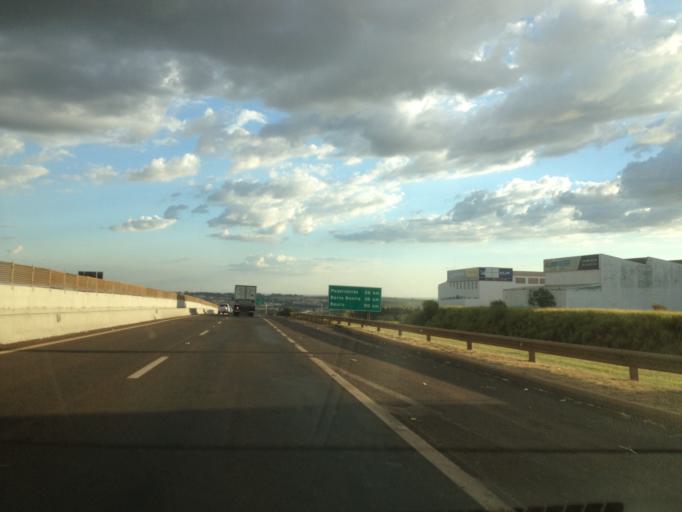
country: BR
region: Sao Paulo
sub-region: Jau
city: Jau
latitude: -22.2671
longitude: -48.5032
